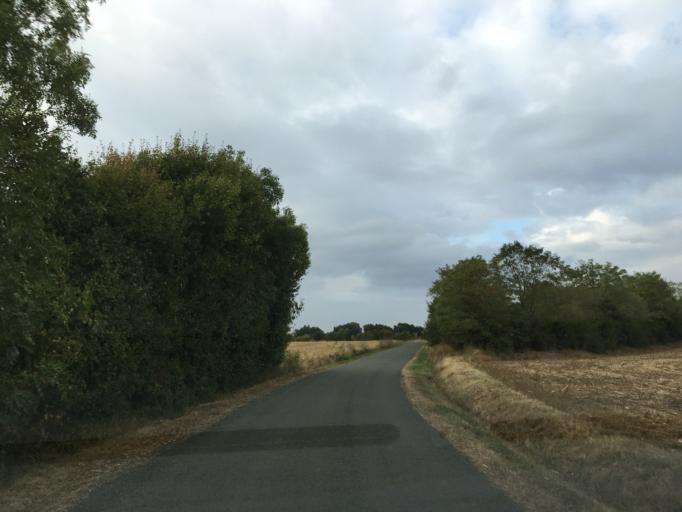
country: FR
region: Poitou-Charentes
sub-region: Departement des Deux-Sevres
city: Beauvoir-sur-Niort
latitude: 46.0851
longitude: -0.4998
